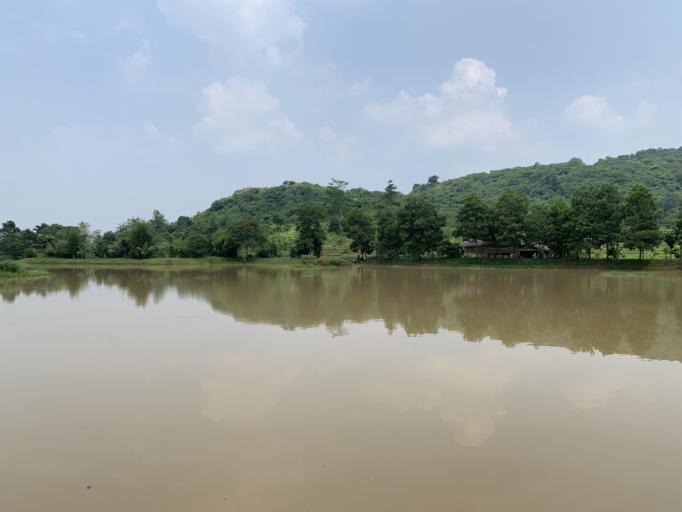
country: ID
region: West Java
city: Serpong
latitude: -6.3795
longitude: 106.5855
